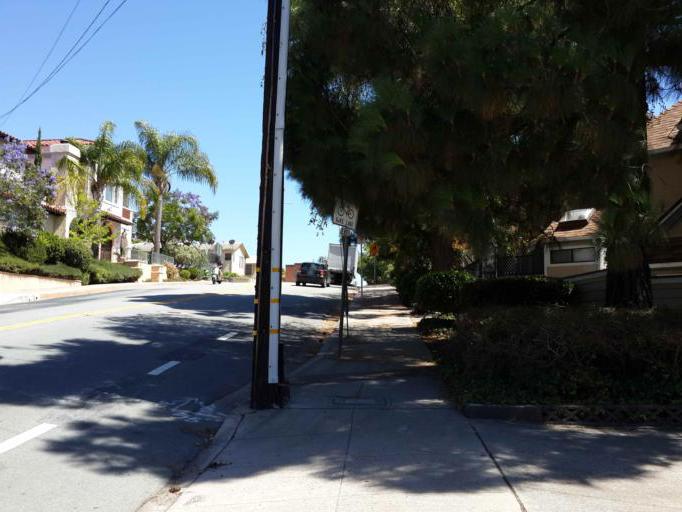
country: US
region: California
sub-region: San Luis Obispo County
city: San Luis Obispo
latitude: 35.2827
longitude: -120.6655
